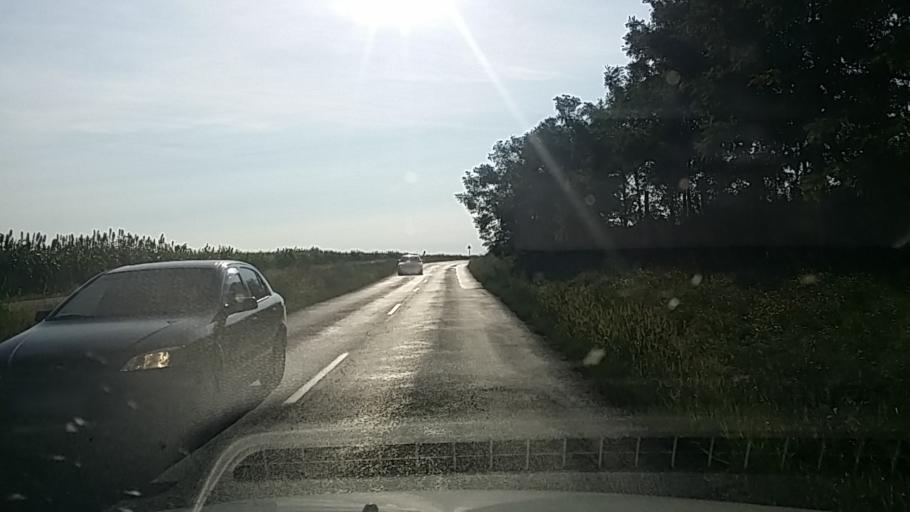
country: HU
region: Gyor-Moson-Sopron
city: Fertod
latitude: 47.6187
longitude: 16.8074
